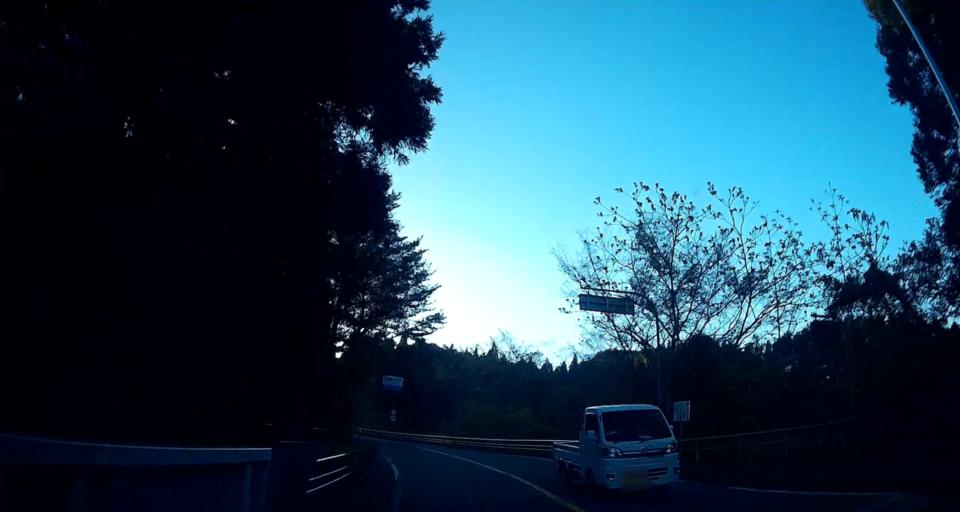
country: JP
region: Iwate
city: Miyako
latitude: 39.6524
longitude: 141.9688
